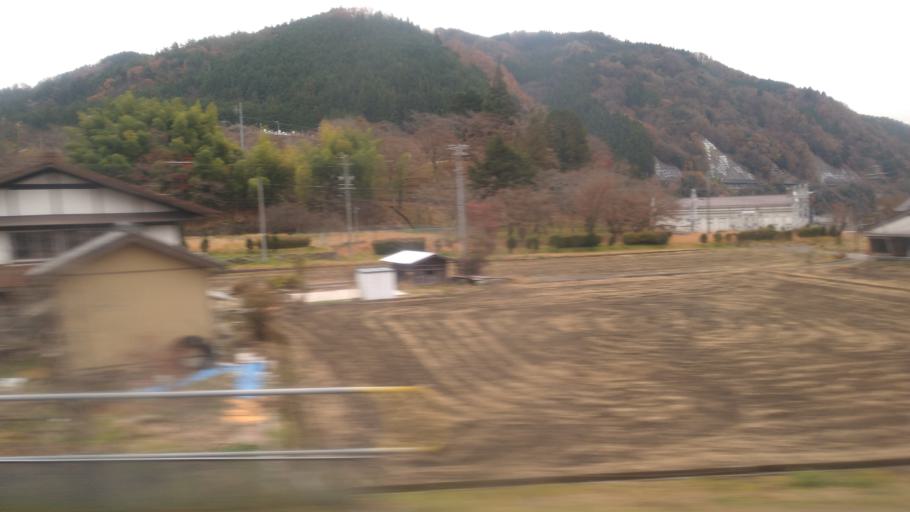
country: JP
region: Gifu
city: Nakatsugawa
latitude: 35.5827
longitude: 137.5344
